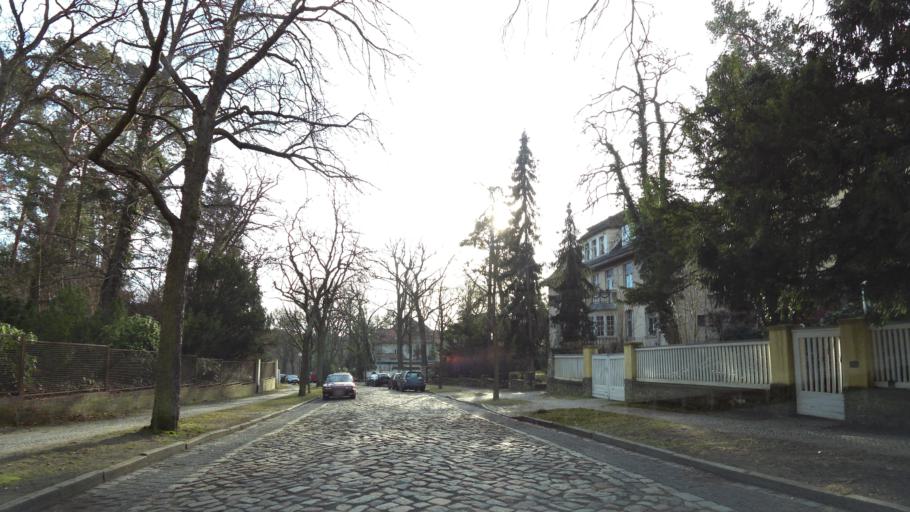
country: DE
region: Berlin
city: Nikolassee
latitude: 52.4267
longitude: 13.1988
